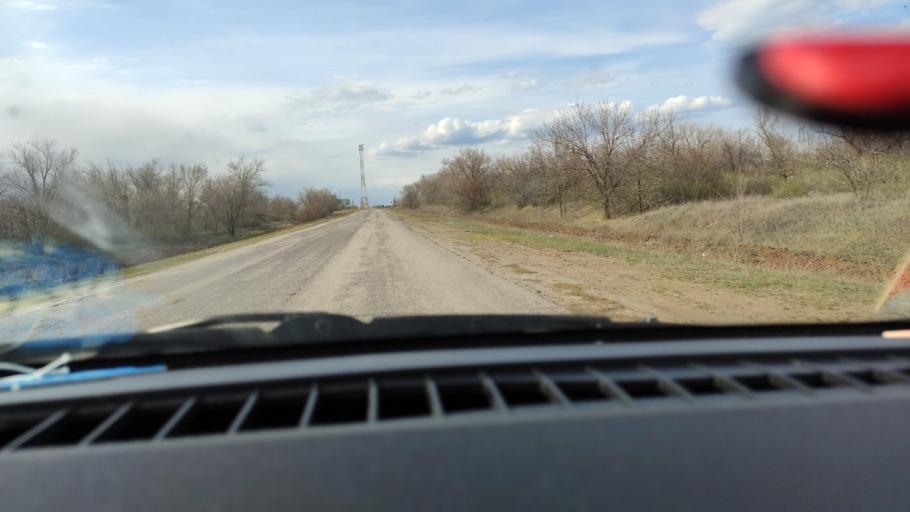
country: RU
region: Saratov
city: Rovnoye
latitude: 51.0208
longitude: 46.0930
